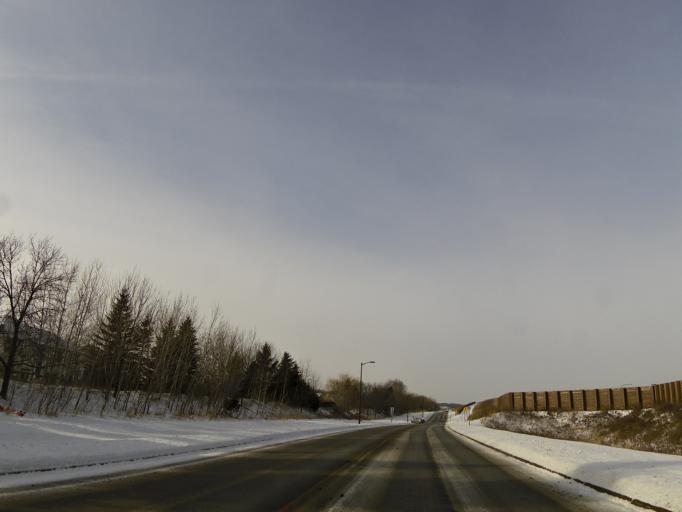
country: US
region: Minnesota
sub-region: Hennepin County
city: Eden Prairie
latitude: 44.8495
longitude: -93.4883
